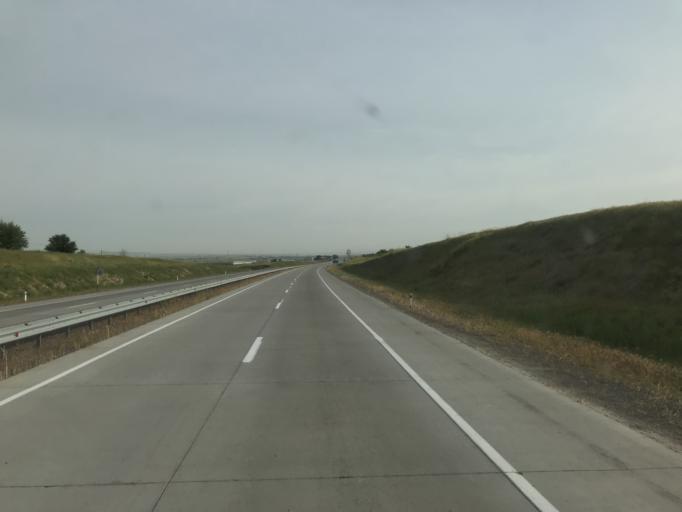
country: KZ
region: Ongtustik Qazaqstan
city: Qazyqurt
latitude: 41.6775
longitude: 69.3937
